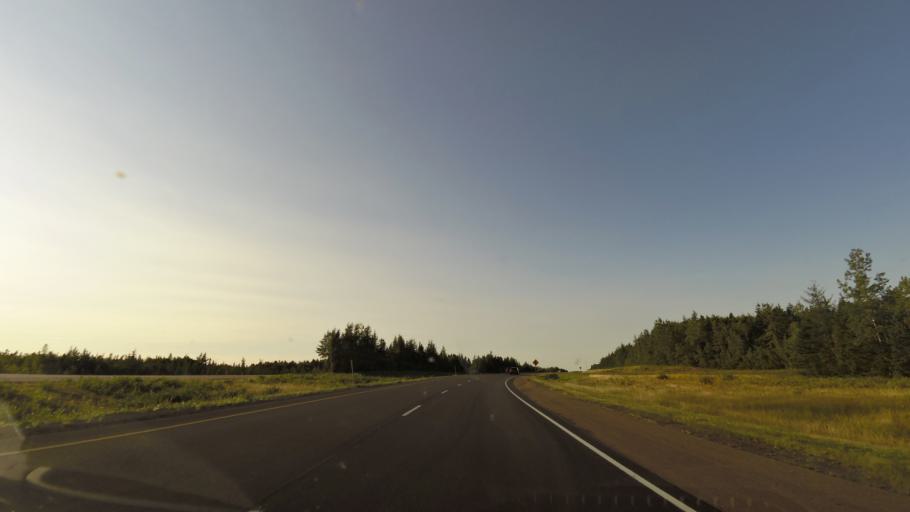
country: CA
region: New Brunswick
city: Dieppe
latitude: 46.0513
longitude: -64.5853
